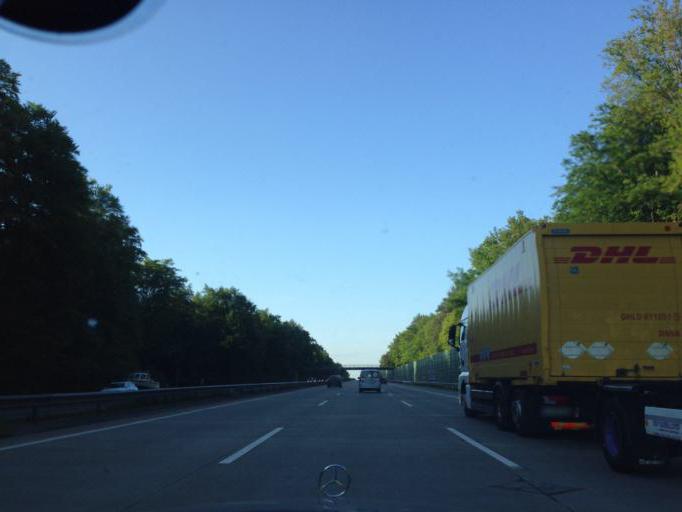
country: DE
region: Schleswig-Holstein
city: Grosshansdorf
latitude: 53.6580
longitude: 10.2976
